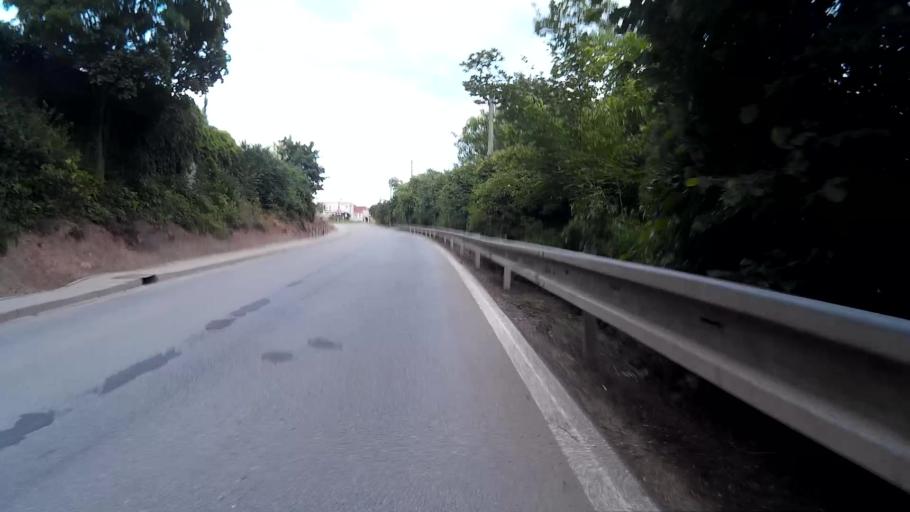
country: CZ
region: South Moravian
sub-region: Okres Brno-Venkov
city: Rosice
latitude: 49.1854
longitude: 16.3845
